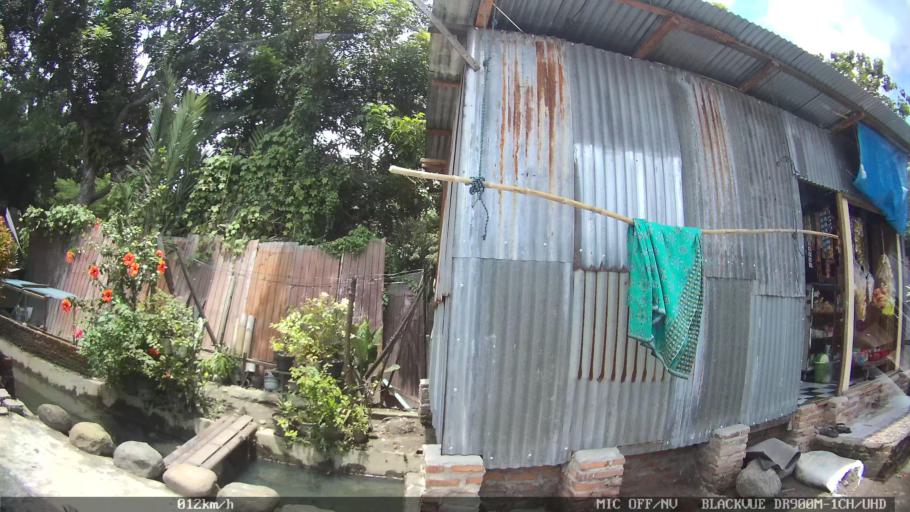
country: ID
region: North Sumatra
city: Medan
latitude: 3.6081
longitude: 98.7219
